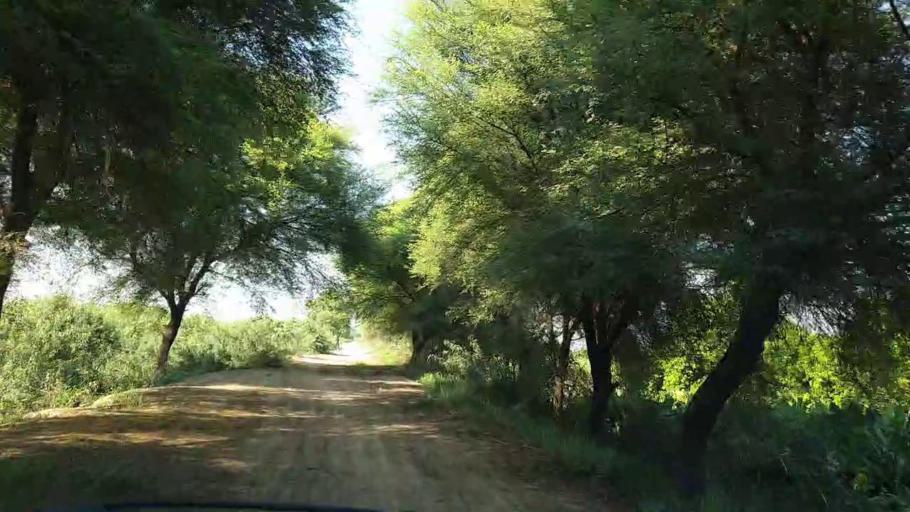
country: PK
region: Sindh
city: Tando Jam
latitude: 25.3629
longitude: 68.5695
